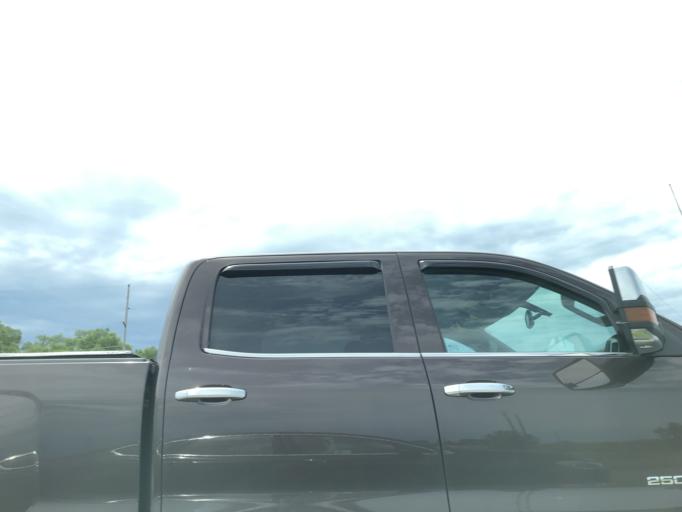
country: US
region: Minnesota
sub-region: Stearns County
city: Saint Augusta
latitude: 45.4636
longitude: -94.1296
